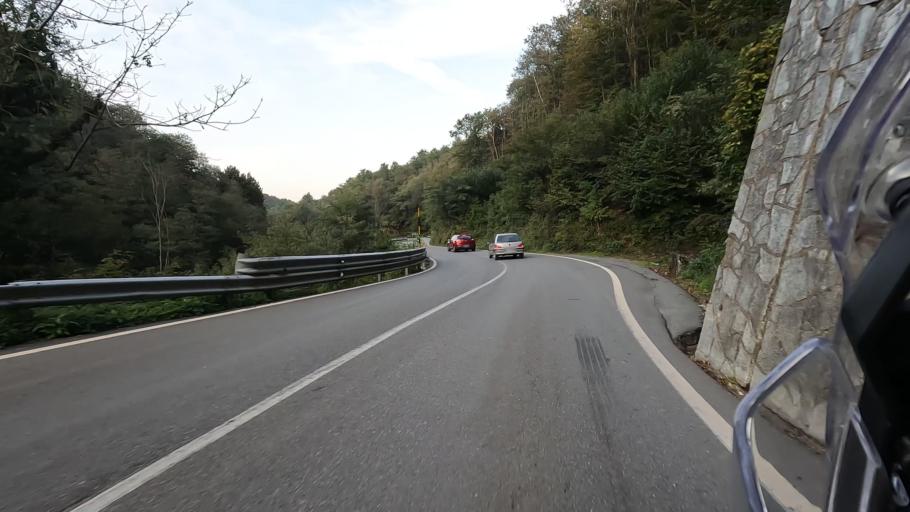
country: IT
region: Liguria
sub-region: Provincia di Savona
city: Osteria dei Cacciatori-Stella
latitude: 44.4540
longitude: 8.4796
